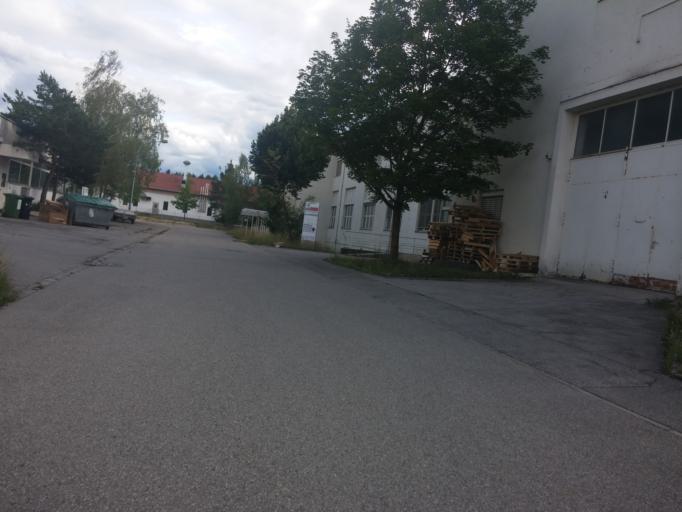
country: DE
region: Bavaria
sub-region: Upper Bavaria
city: Ottobrunn
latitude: 48.0411
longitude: 11.6639
